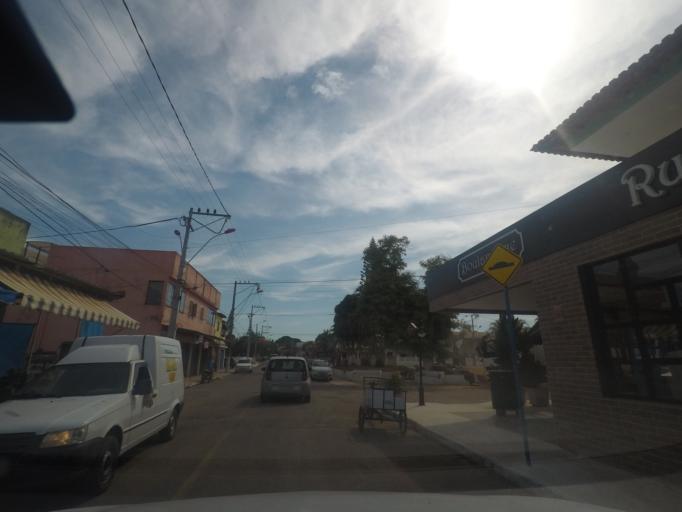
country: BR
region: Rio de Janeiro
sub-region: Marica
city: Marica
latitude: -22.9554
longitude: -42.8122
